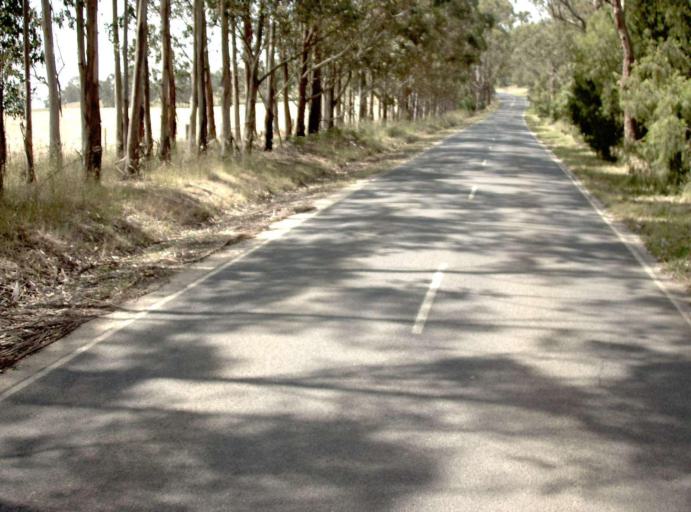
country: AU
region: Victoria
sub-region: Latrobe
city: Traralgon
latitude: -38.2808
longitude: 146.5470
